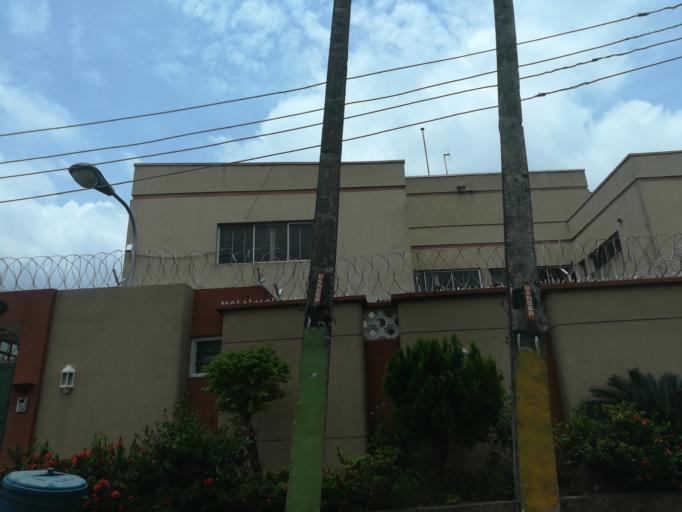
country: NG
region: Lagos
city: Oshodi
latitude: 6.5433
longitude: 3.3308
